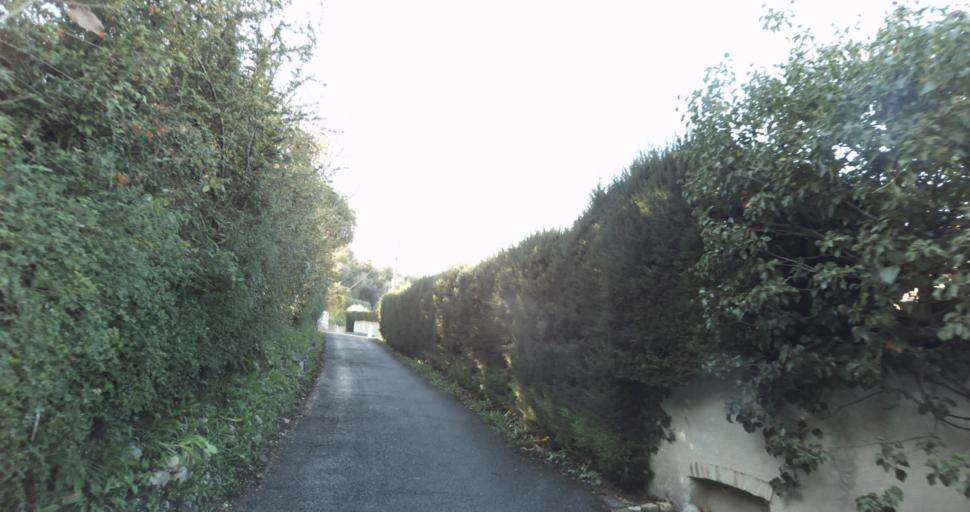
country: FR
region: Provence-Alpes-Cote d'Azur
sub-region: Departement des Alpes-Maritimes
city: La Gaude
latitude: 43.7166
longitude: 7.1373
